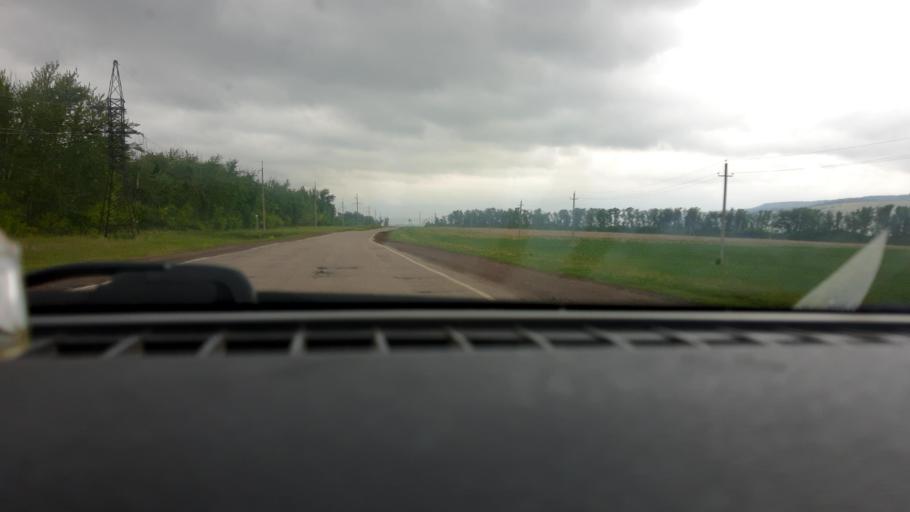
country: RU
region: Bashkortostan
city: Kandry
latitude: 54.3468
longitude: 54.0431
